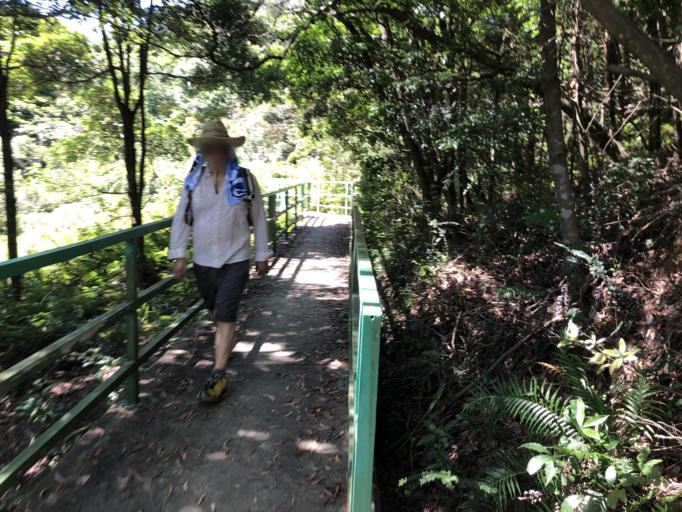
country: HK
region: Tuen Mun
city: Tuen Mun
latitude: 22.2803
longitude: 113.9852
